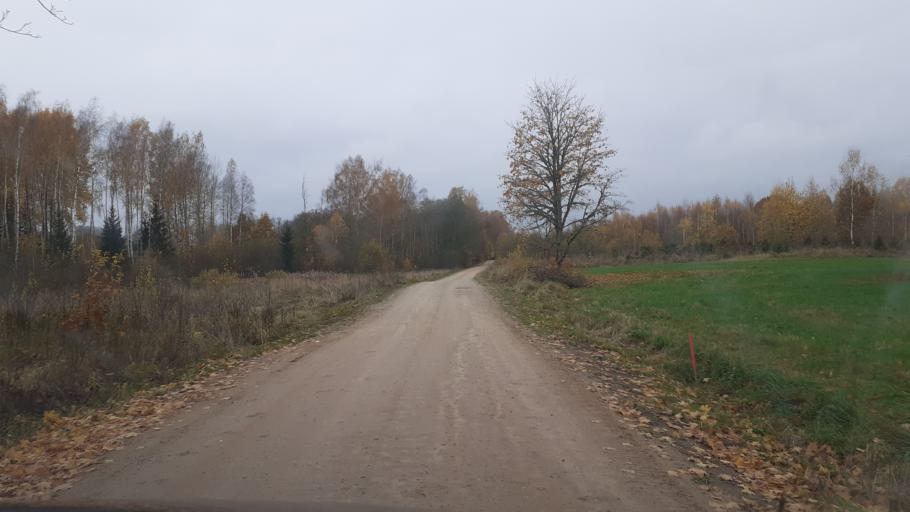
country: LV
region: Saldus Rajons
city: Saldus
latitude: 56.8765
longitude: 22.3038
